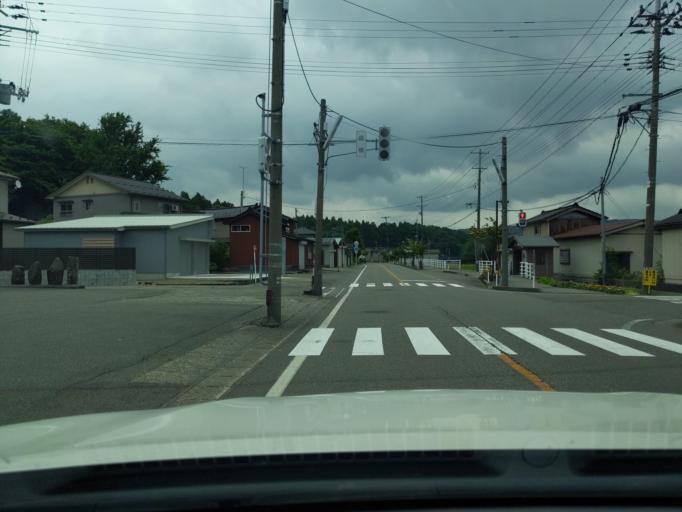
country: JP
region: Niigata
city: Kashiwazaki
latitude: 37.3390
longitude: 138.5720
